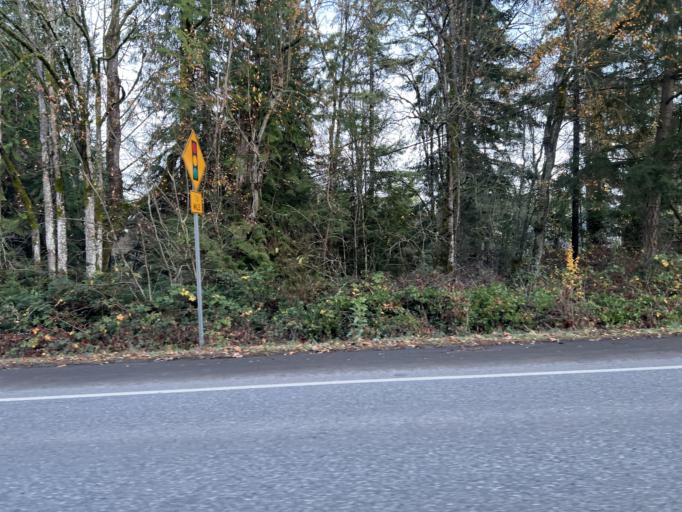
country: US
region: Washington
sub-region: Kitsap County
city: Bainbridge Island
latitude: 47.6460
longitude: -122.5193
